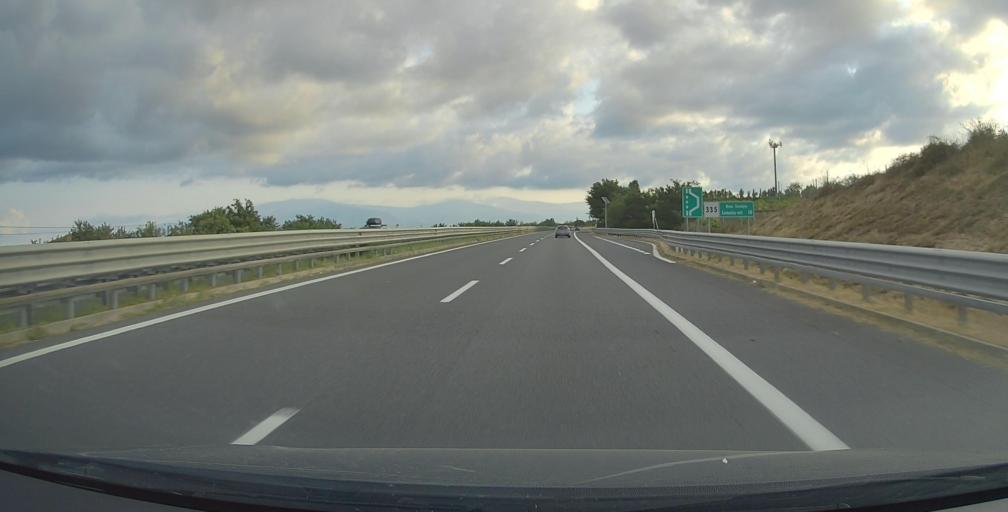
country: IT
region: Calabria
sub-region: Provincia di Catanzaro
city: Acconia
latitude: 38.8132
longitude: 16.2356
